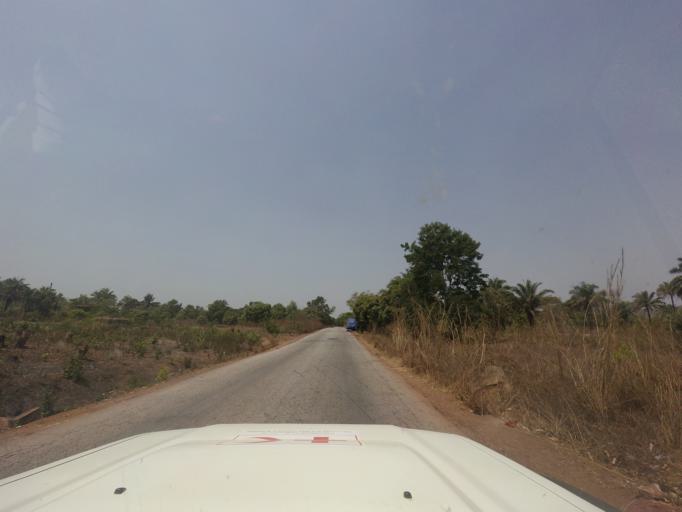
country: GN
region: Kindia
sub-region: Kindia
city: Kindia
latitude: 9.8941
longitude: -13.0501
